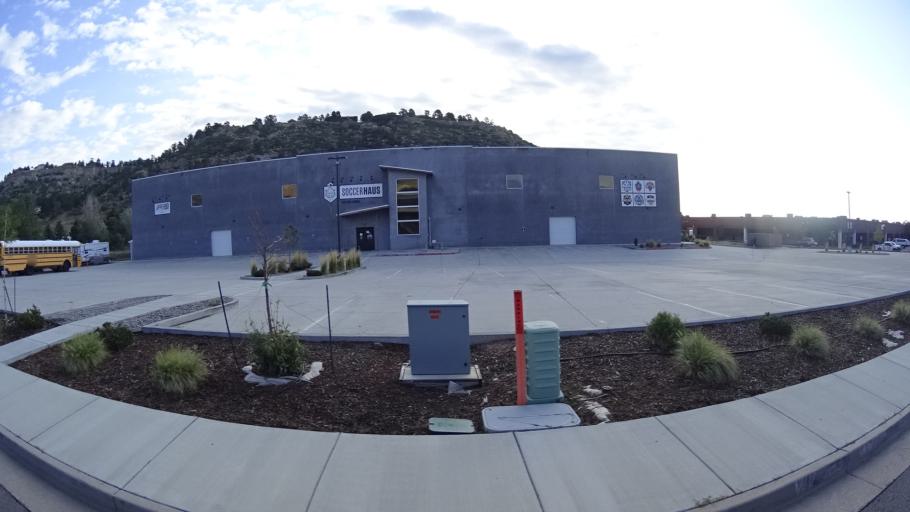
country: US
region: Colorado
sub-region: El Paso County
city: Colorado Springs
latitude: 38.9023
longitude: -104.8525
